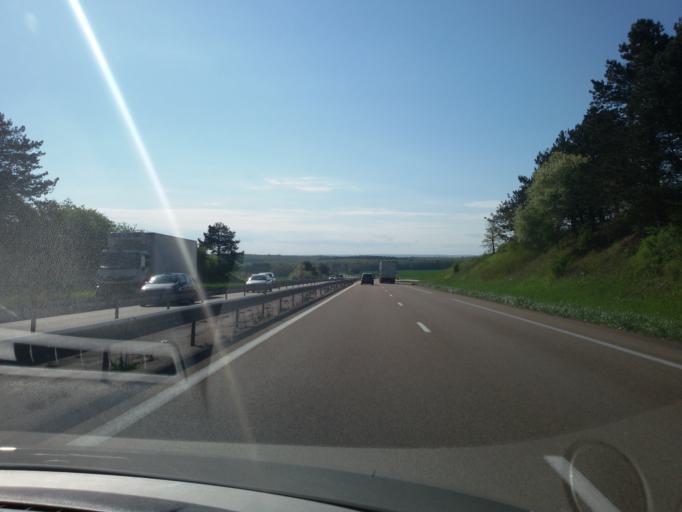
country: FR
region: Bourgogne
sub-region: Departement de l'Yonne
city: Vermenton
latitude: 47.7261
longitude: 3.7497
